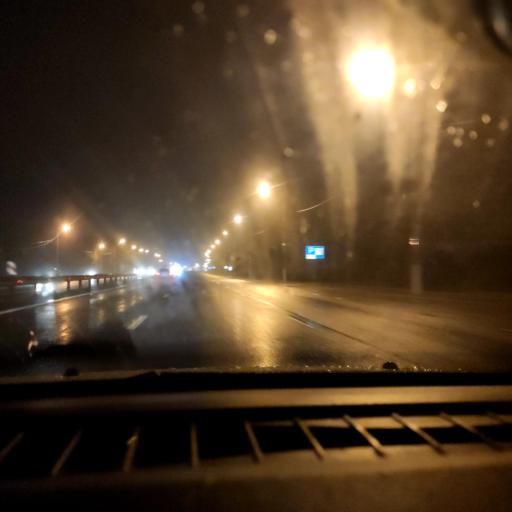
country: RU
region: Voronezj
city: Novaya Usman'
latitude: 51.6222
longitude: 39.3594
